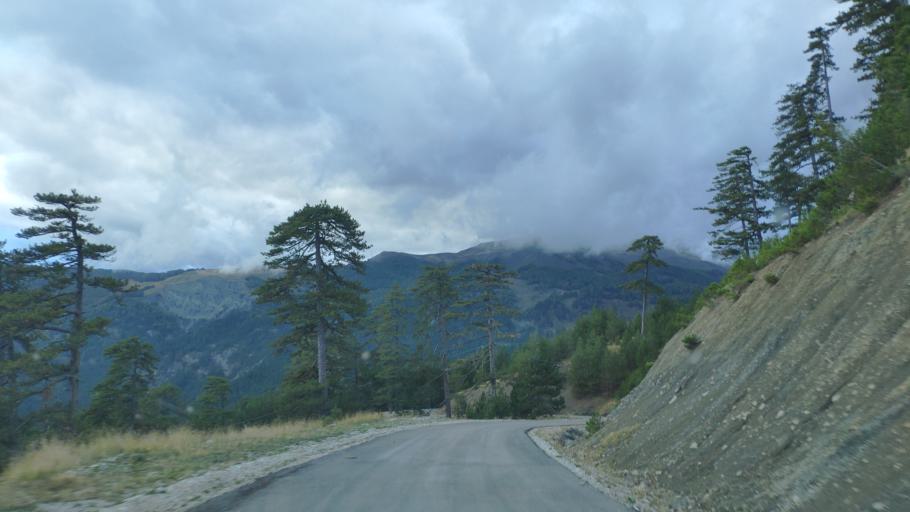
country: AL
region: Korce
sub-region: Rrethi i Kolonjes
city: Erseke
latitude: 40.2917
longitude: 20.8663
